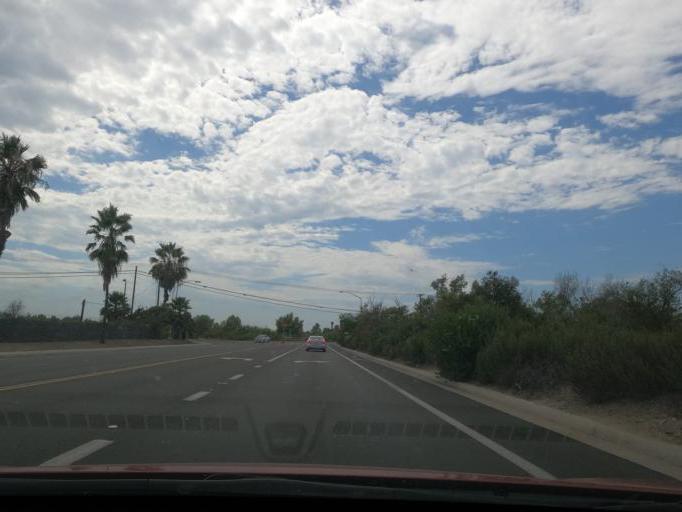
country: US
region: California
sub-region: San Diego County
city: Imperial Beach
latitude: 32.5542
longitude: -117.0615
